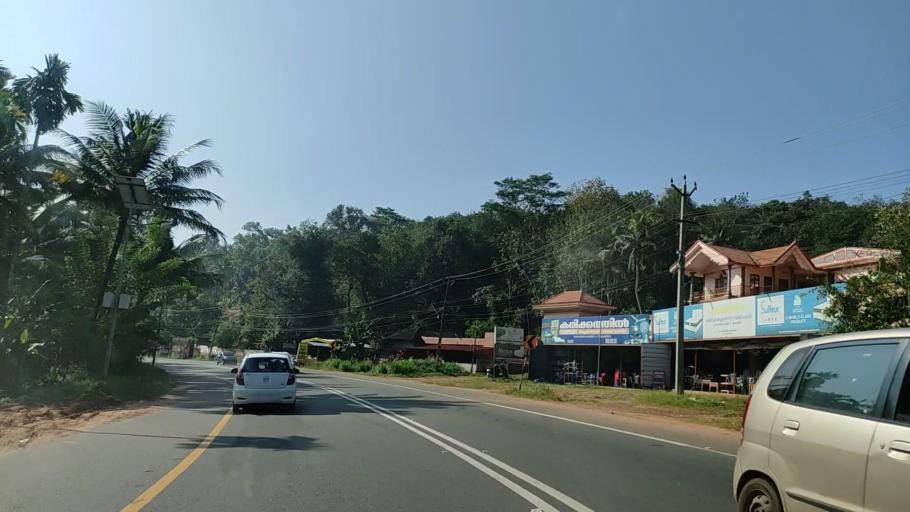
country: IN
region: Kerala
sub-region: Kollam
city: Punalur
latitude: 8.9228
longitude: 76.8536
